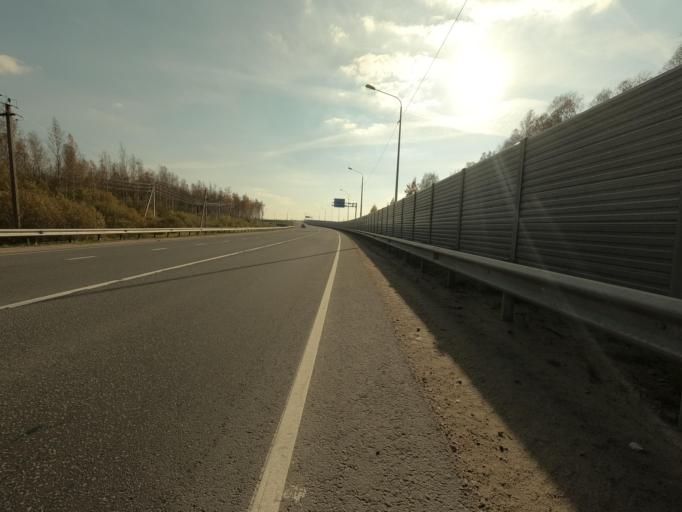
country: RU
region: Leningrad
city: Mga
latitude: 59.7623
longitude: 31.0942
